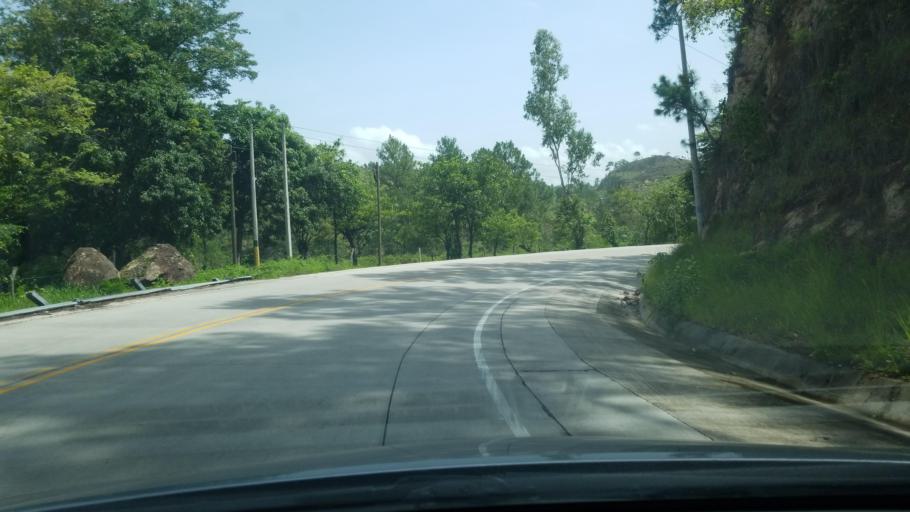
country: HN
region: Copan
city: Florida
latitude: 15.0099
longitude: -88.8361
